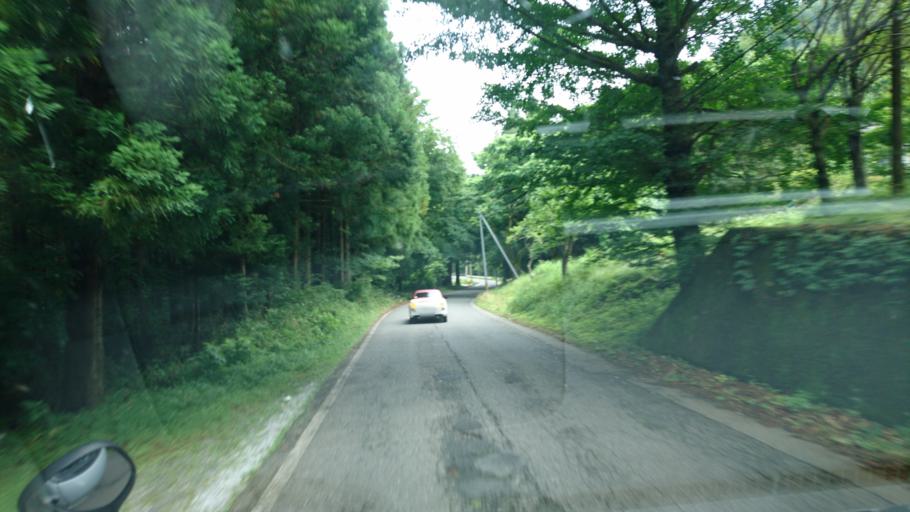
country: JP
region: Iwate
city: Ofunato
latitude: 39.1324
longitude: 141.7927
